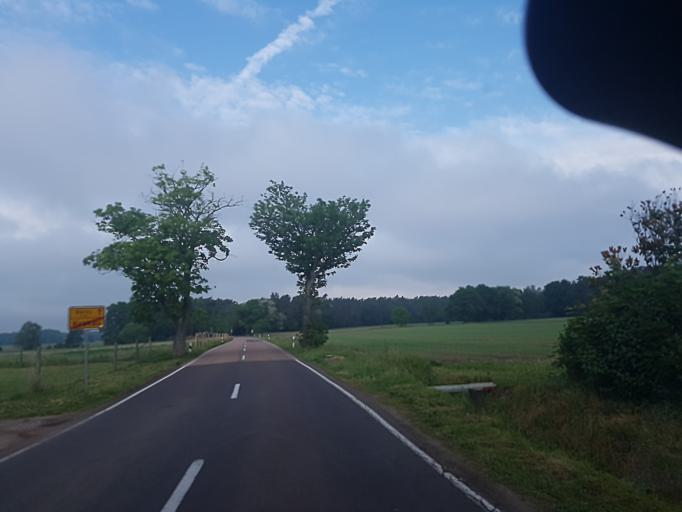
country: DE
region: Saxony-Anhalt
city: Rosslau
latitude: 51.9873
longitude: 12.3027
